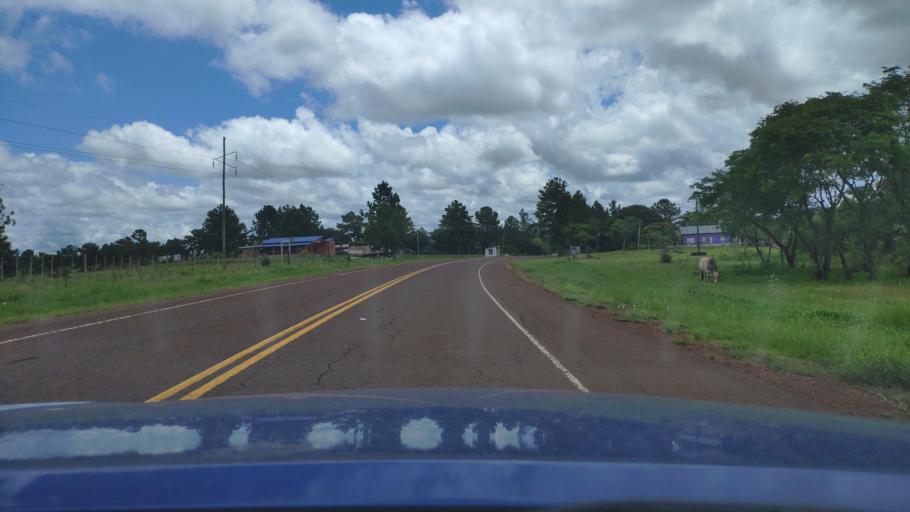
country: AR
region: Misiones
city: Dos Arroyos
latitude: -27.7453
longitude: -55.2647
